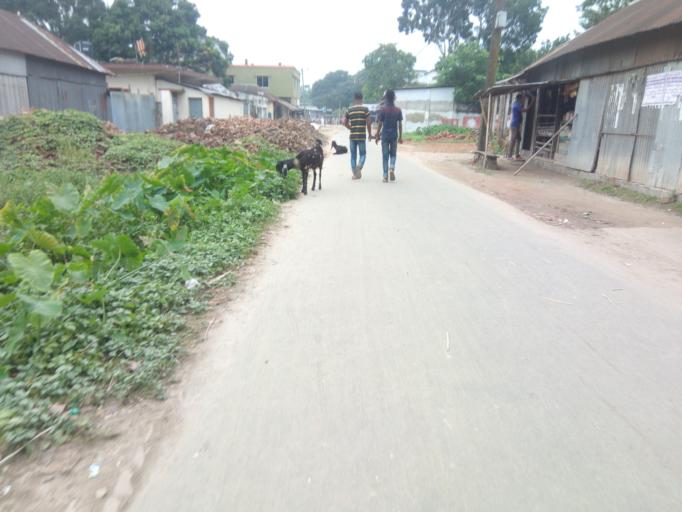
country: BD
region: Khulna
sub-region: Magura
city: Magura
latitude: 23.5443
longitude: 89.6283
